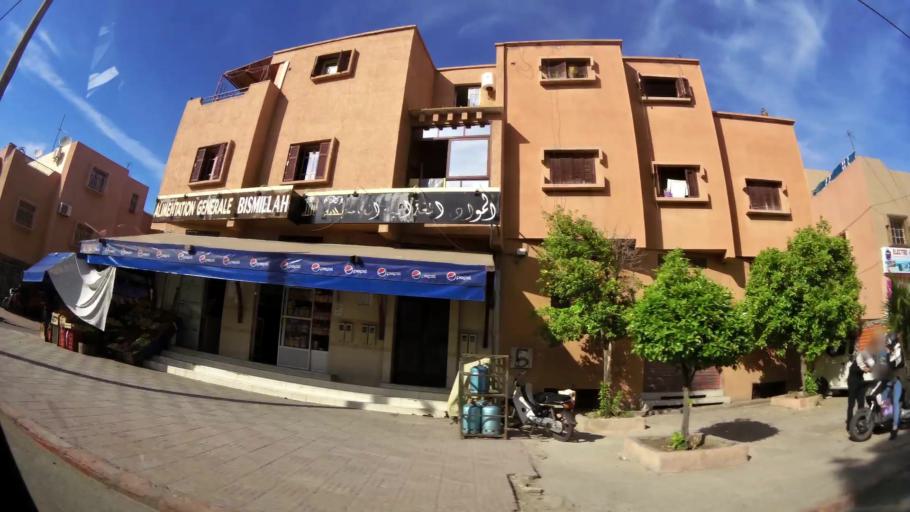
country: MA
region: Marrakech-Tensift-Al Haouz
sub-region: Marrakech
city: Marrakesh
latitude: 31.6564
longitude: -8.0132
